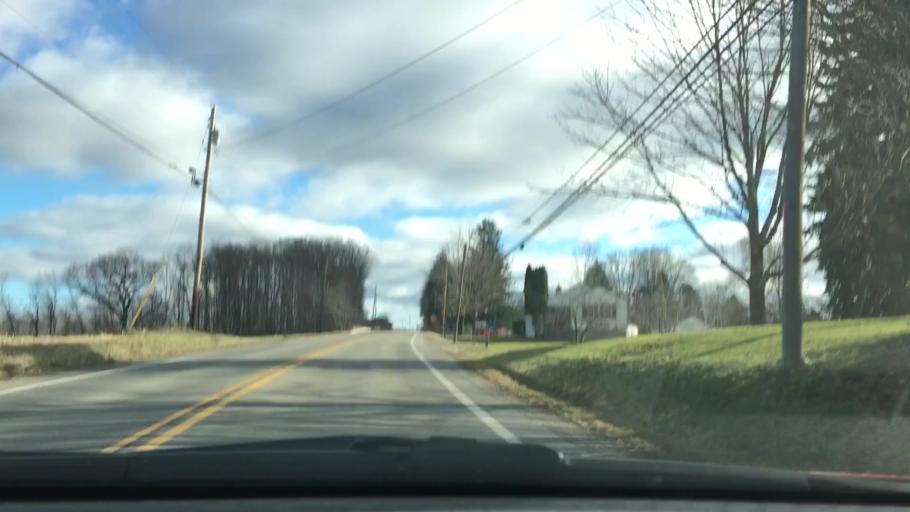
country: US
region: Pennsylvania
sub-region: Westmoreland County
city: Avonmore
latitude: 40.6065
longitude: -79.4484
